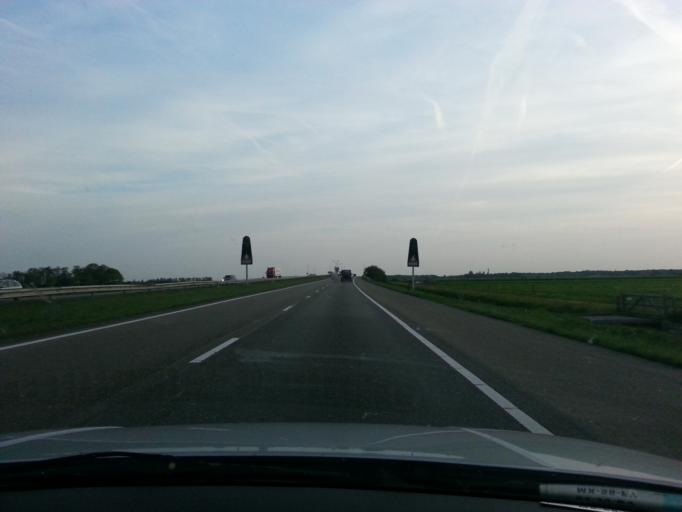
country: NL
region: Friesland
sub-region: Gemeente Skarsterlan
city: Joure
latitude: 52.9436
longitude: 5.7974
